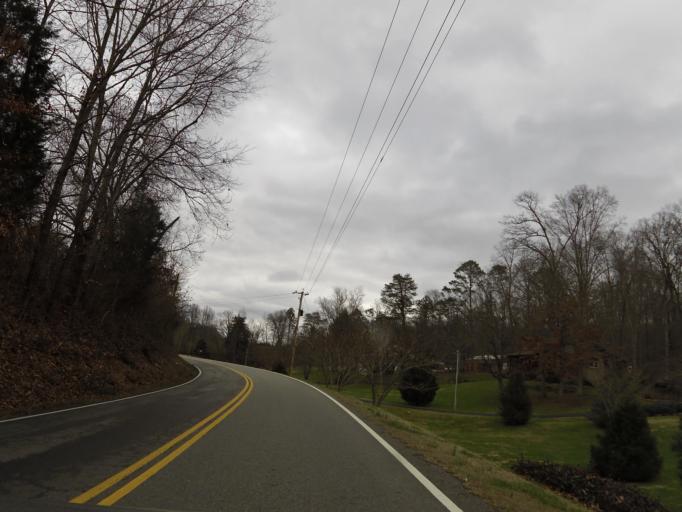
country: US
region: Tennessee
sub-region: Grainger County
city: Blaine
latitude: 36.1515
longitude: -83.6304
